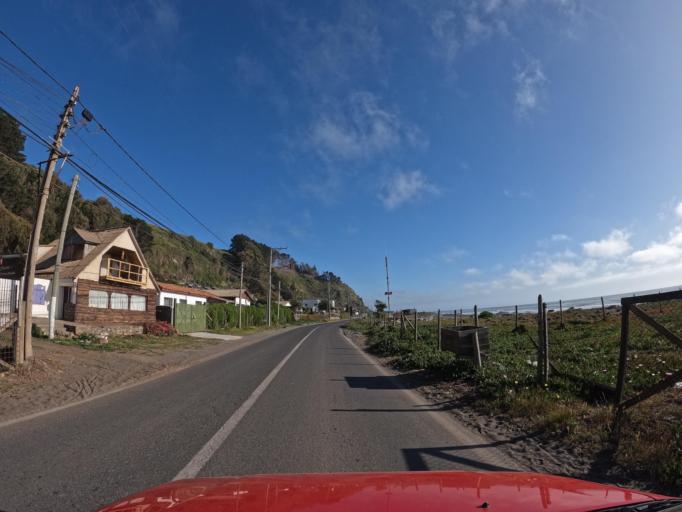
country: CL
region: Maule
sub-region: Provincia de Talca
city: Constitucion
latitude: -34.9115
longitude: -72.1815
